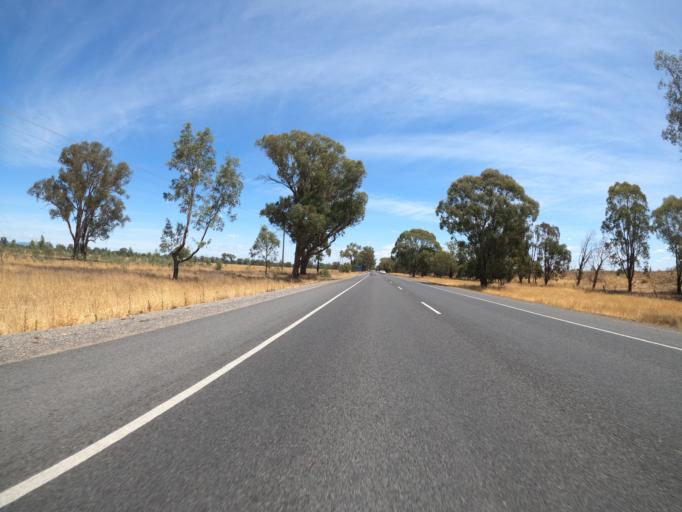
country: AU
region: Victoria
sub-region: Benalla
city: Benalla
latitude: -36.5272
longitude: 146.0481
